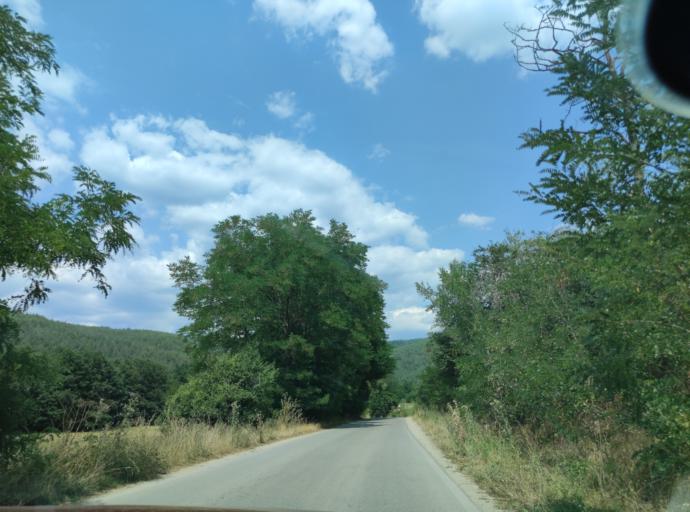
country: BG
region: Blagoevgrad
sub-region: Obshtina Belitsa
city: Belitsa
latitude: 41.9798
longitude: 23.5529
